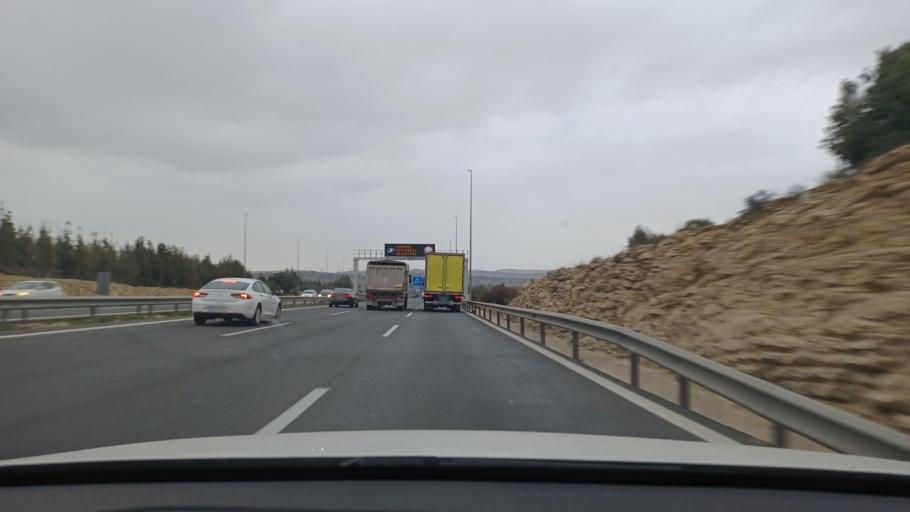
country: ES
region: Valencia
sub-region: Provincia de Alicante
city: Monforte del Cid
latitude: 38.3589
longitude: -0.6789
